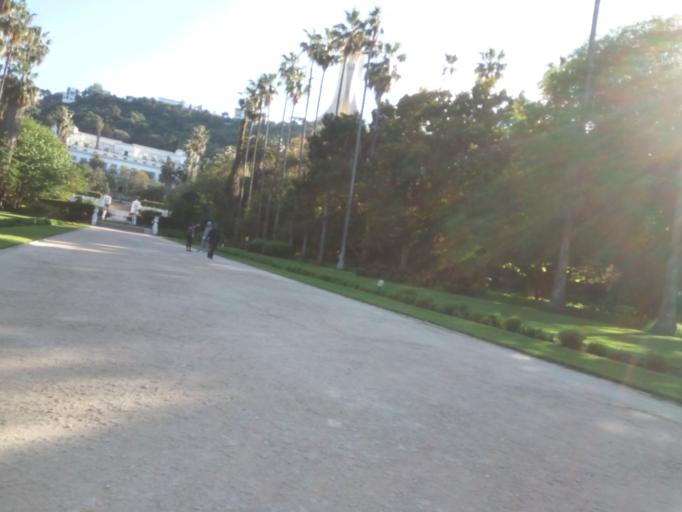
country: DZ
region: Alger
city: Algiers
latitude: 36.7489
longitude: 3.0741
